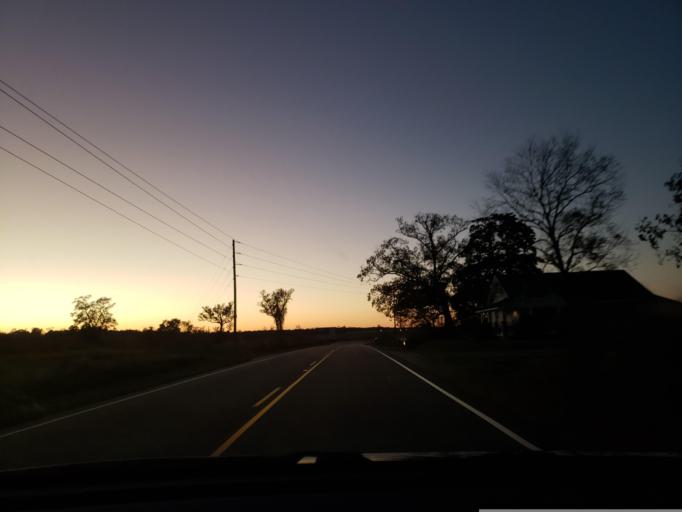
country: US
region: North Carolina
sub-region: Duplin County
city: Kenansville
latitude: 34.8879
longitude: -77.9026
